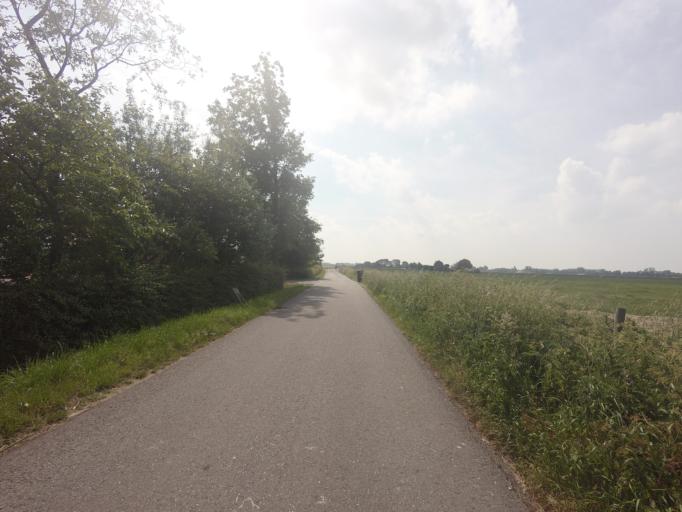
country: NL
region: Utrecht
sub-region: Gemeente IJsselstein
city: IJsselstein
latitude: 52.0033
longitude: 5.0595
